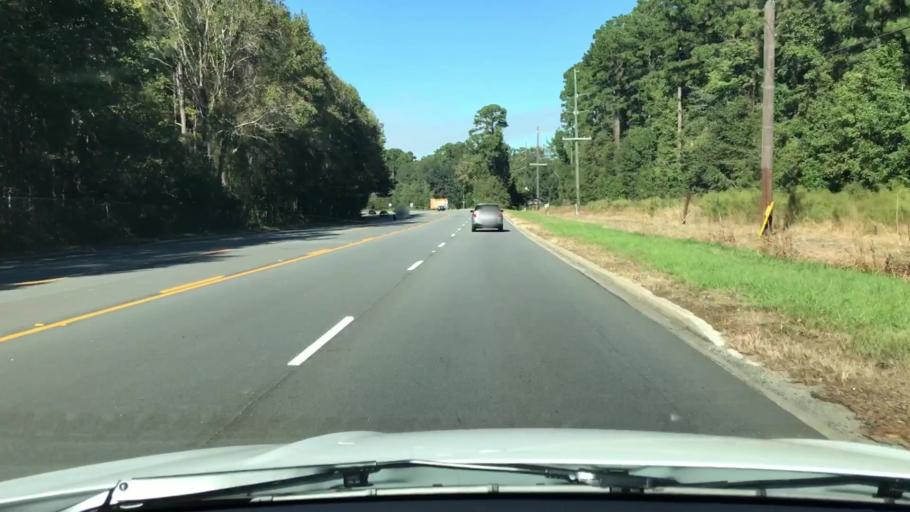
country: US
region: South Carolina
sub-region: Beaufort County
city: Laurel Bay
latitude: 32.5826
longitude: -80.7430
